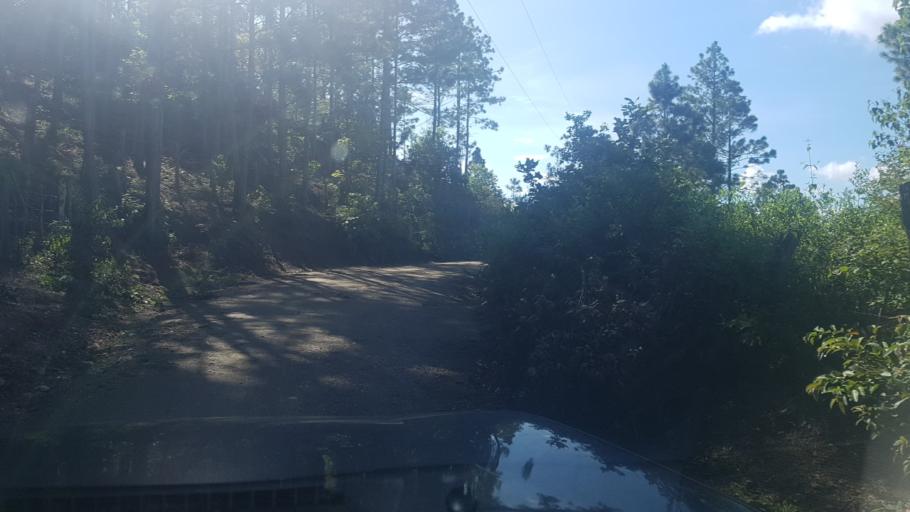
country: NI
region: Nueva Segovia
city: Ocotal
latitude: 13.6429
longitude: -86.6404
